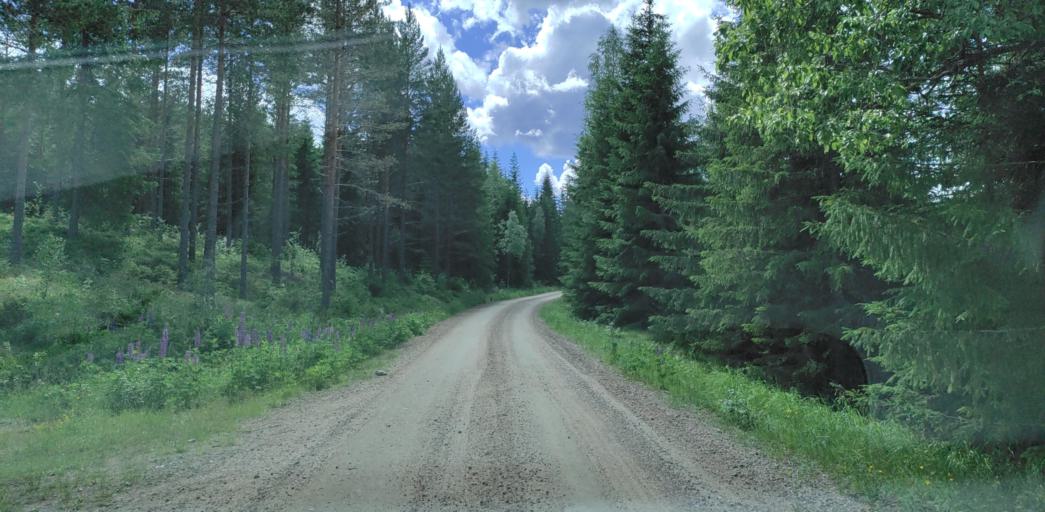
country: SE
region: Vaermland
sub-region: Hagfors Kommun
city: Ekshaerad
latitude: 60.0961
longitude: 13.3469
